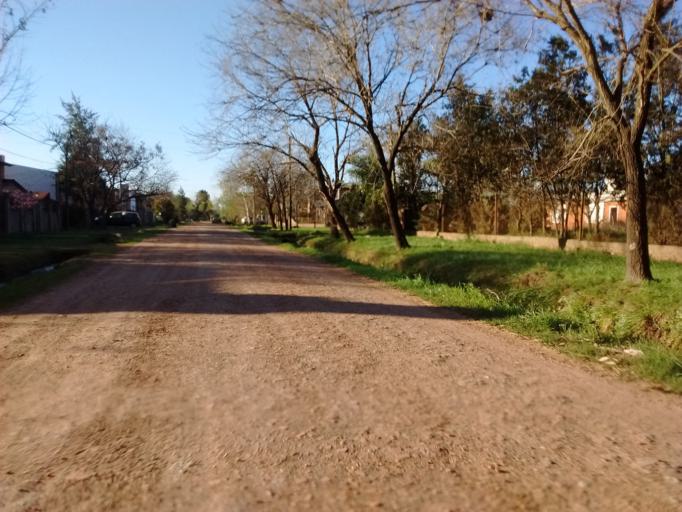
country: AR
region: Santa Fe
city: Funes
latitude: -32.9275
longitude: -60.7918
